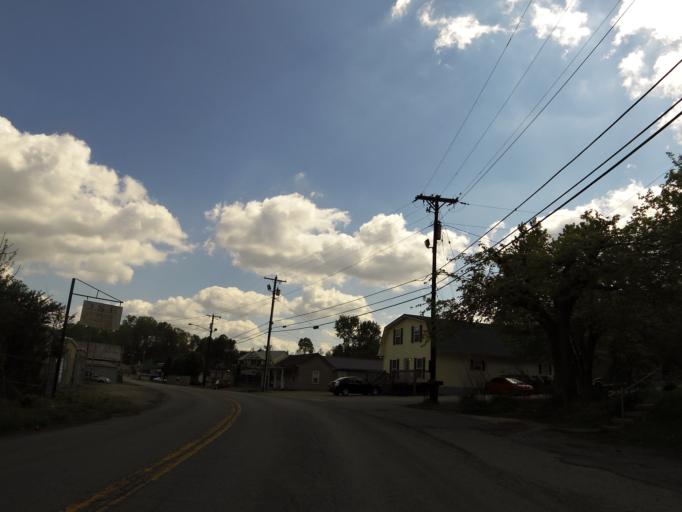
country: US
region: Kentucky
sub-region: Bell County
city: Middlesboro
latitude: 36.6258
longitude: -83.7163
